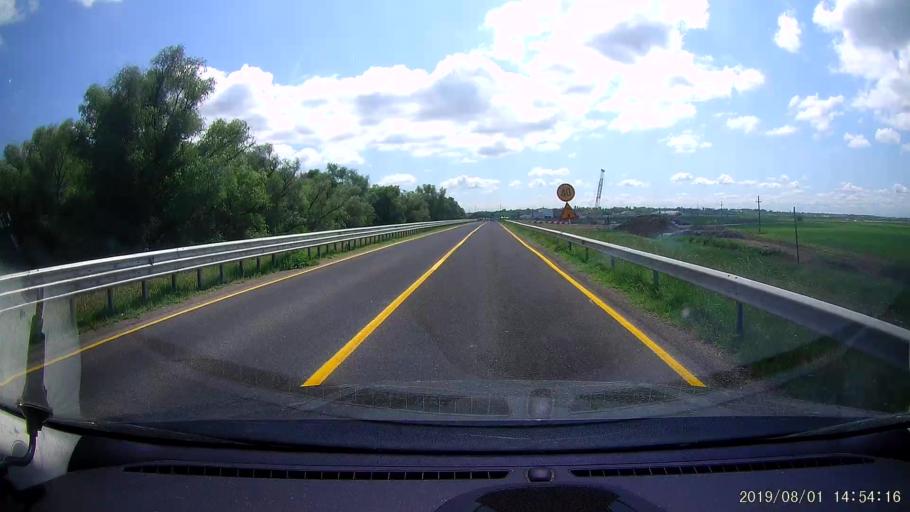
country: RO
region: Braila
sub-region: Municipiul Braila
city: Braila
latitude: 45.3206
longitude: 27.9916
